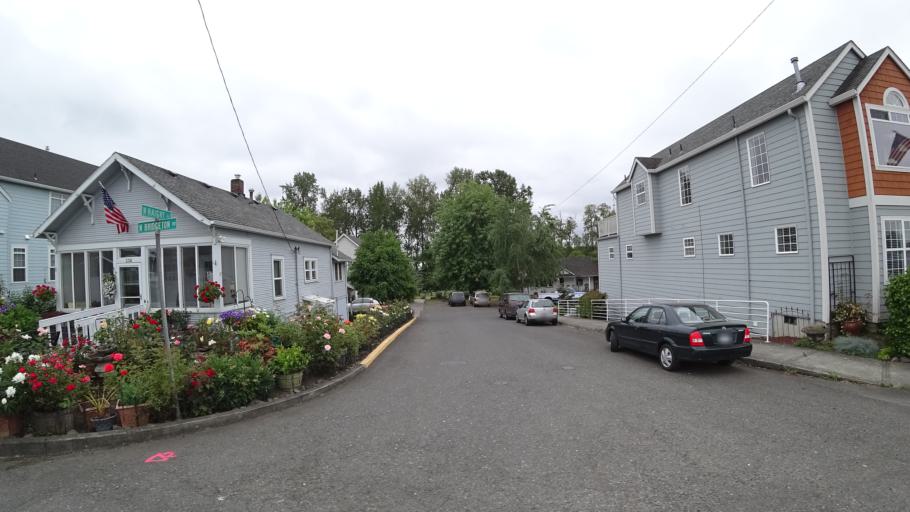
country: US
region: Washington
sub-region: Clark County
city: Vancouver
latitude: 45.6032
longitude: -122.6699
